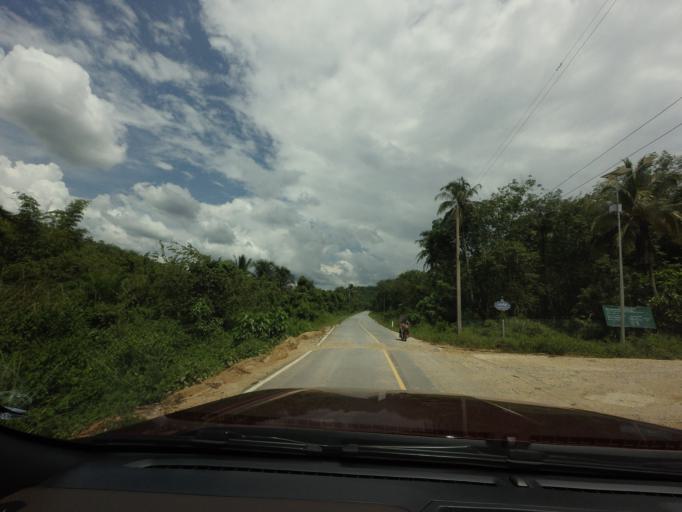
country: TH
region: Narathiwat
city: Chanae
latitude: 6.0550
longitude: 101.6876
